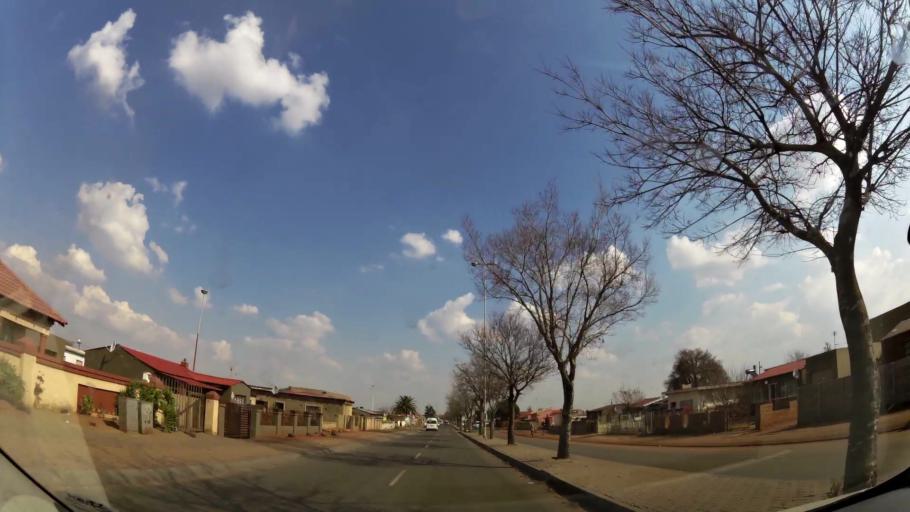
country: ZA
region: Gauteng
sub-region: Ekurhuleni Metropolitan Municipality
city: Germiston
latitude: -26.3235
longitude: 28.1557
